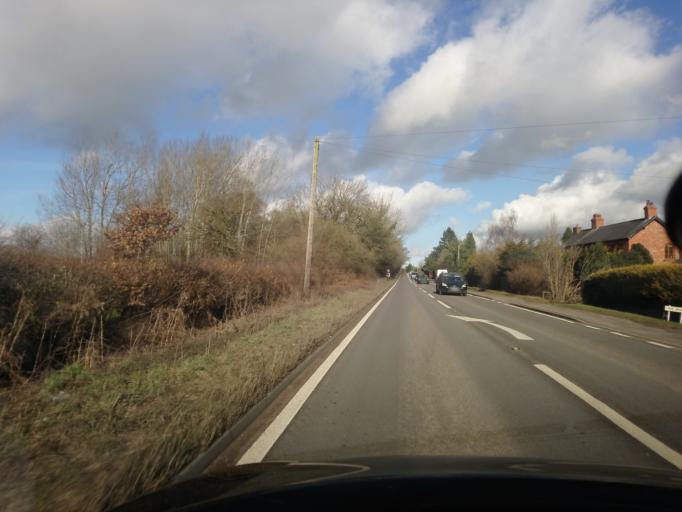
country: GB
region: England
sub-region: Shropshire
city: Astley
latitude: 52.7554
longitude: -2.7165
